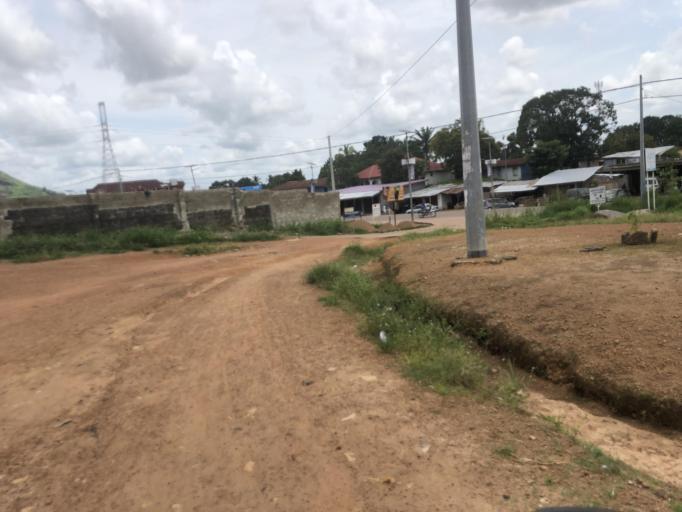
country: SL
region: Northern Province
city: Makeni
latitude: 8.8822
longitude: -12.0528
